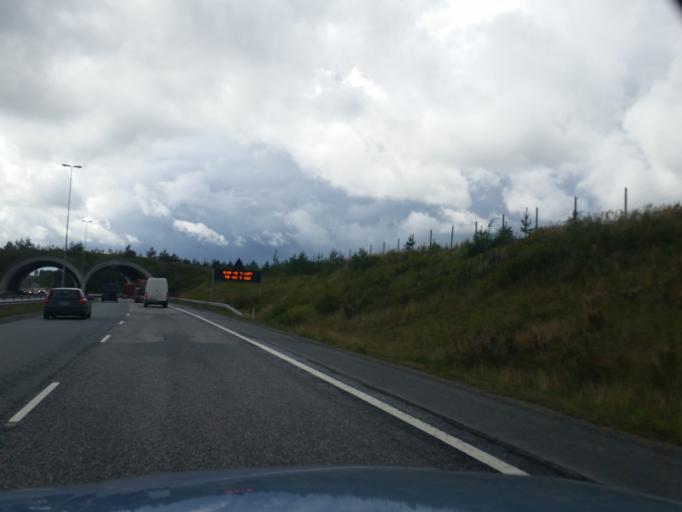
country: FI
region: Uusimaa
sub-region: Helsinki
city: Lohja
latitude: 60.3006
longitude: 24.1930
